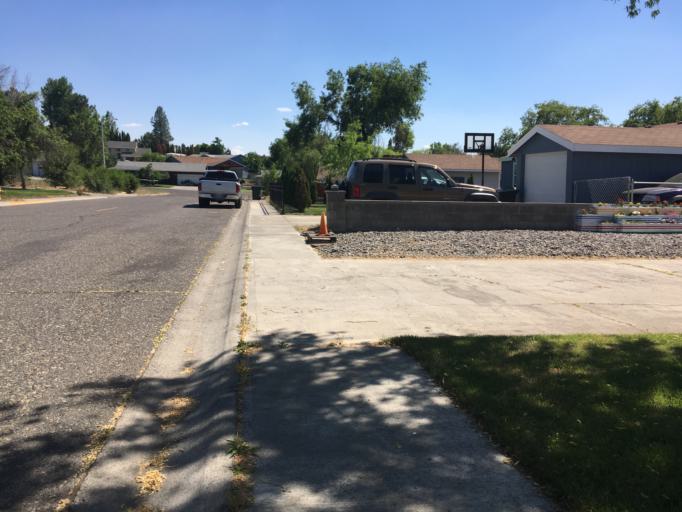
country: US
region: Oregon
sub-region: Morrow County
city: Boardman
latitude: 45.8325
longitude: -119.7088
